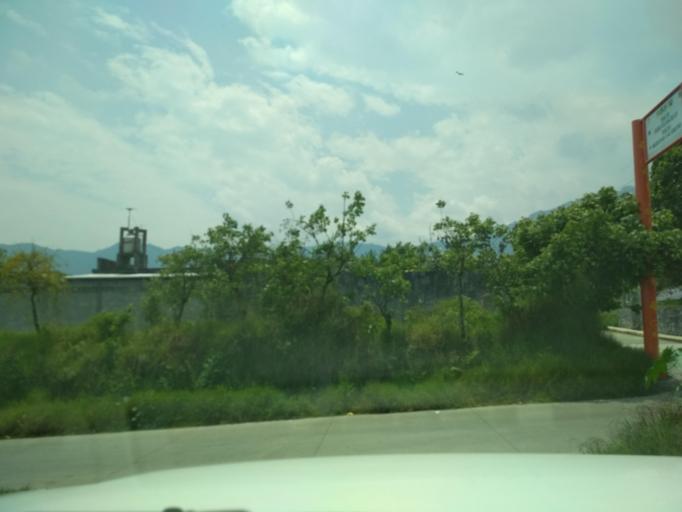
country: MX
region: Veracruz
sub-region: Mariano Escobedo
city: Mariano Escobedo
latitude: 18.9077
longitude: -97.1277
